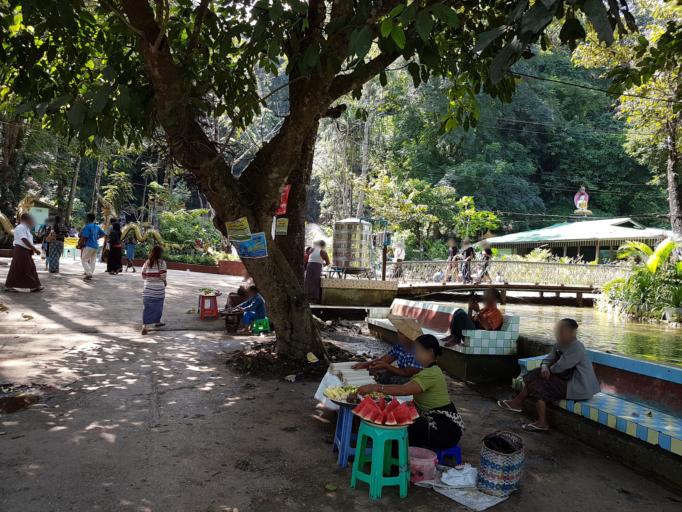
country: MM
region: Mandalay
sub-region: Pyin Oo Lwin District
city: Pyin Oo Lwin
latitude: 22.0964
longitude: 96.6203
